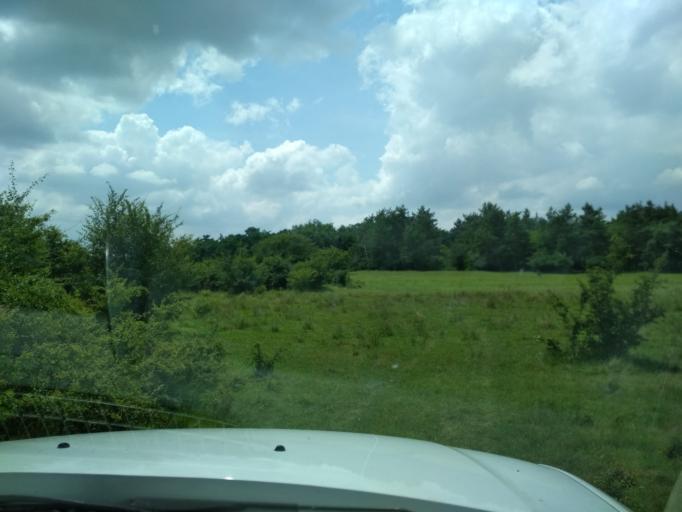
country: HU
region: Pest
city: Tapiosag
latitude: 47.4160
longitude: 19.6546
